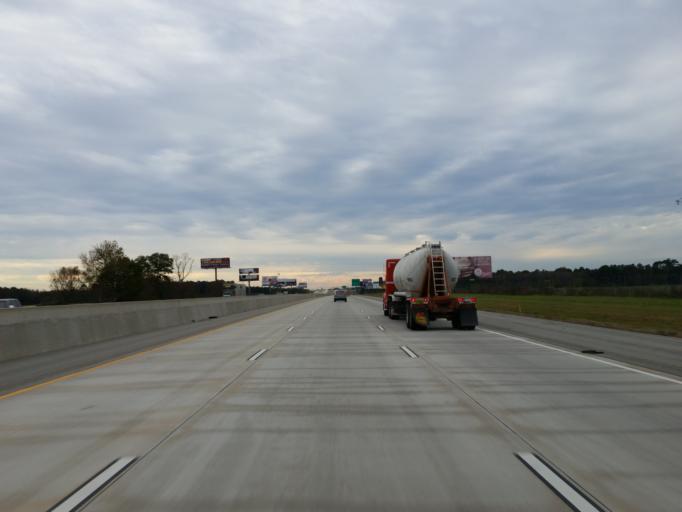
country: US
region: Georgia
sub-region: Cook County
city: Sparks
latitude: 31.1809
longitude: -83.4529
